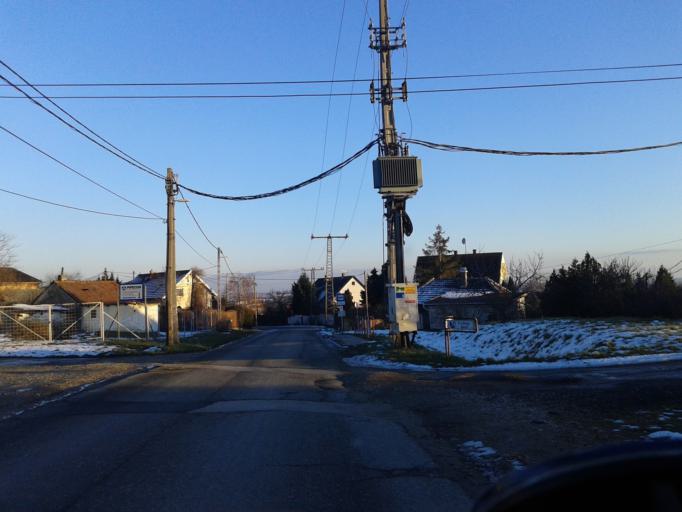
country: HU
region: Pest
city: Diosd
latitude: 47.4157
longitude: 18.9467
